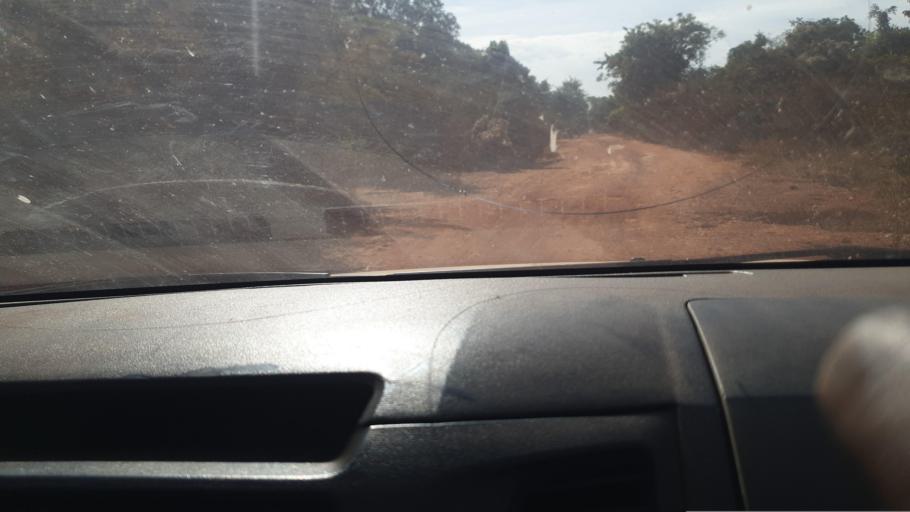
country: ML
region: Sikasso
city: Sikasso
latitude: 11.8336
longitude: -6.0074
